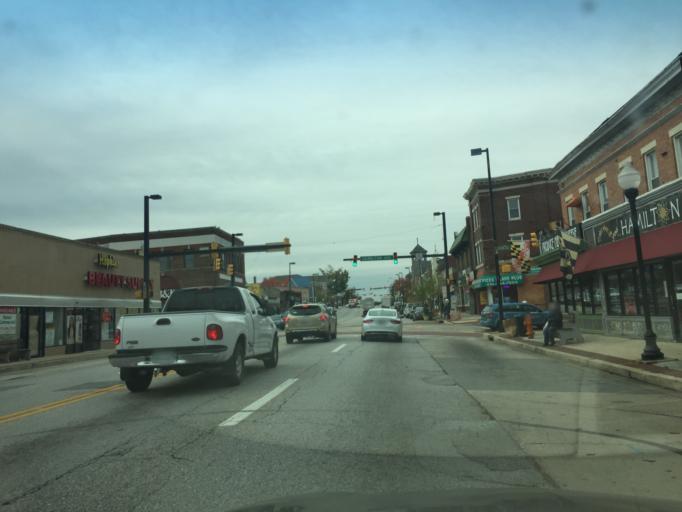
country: US
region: Maryland
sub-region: Baltimore County
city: Parkville
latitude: 39.3526
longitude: -76.5613
